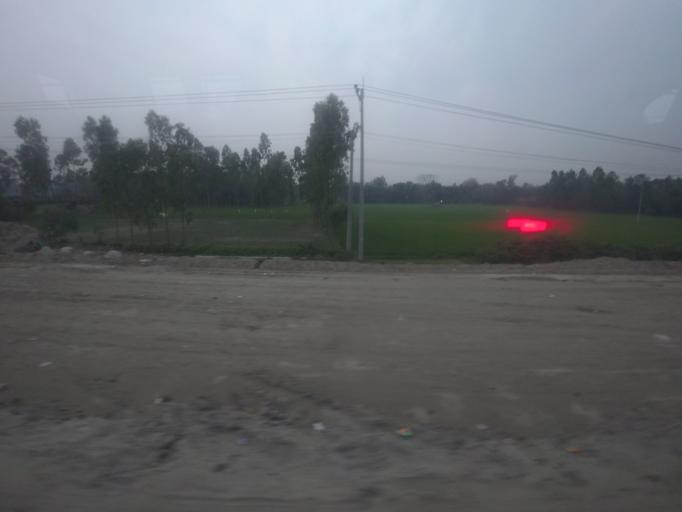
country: BD
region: Dhaka
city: Tangail
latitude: 24.3255
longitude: 89.9246
